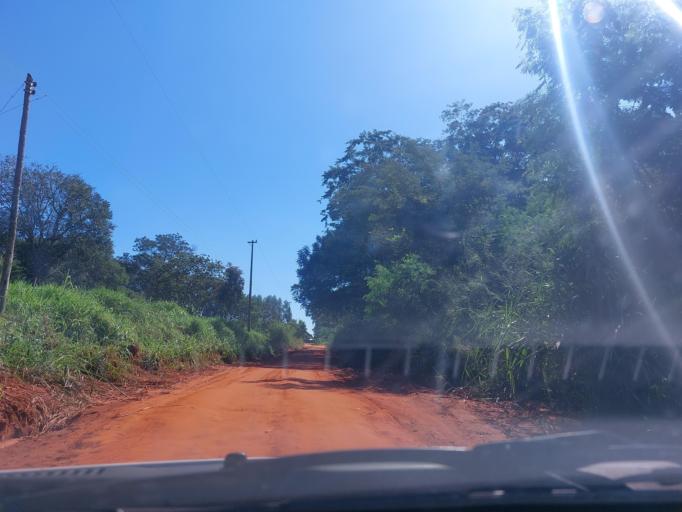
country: PY
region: San Pedro
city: Lima
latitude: -24.1656
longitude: -56.0134
